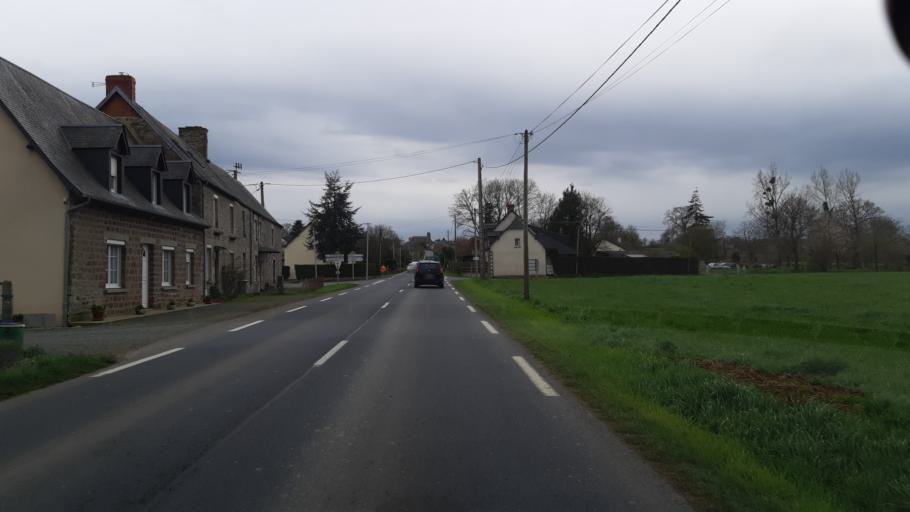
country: FR
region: Lower Normandy
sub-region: Departement de la Manche
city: Percy
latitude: 48.9687
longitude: -1.1640
